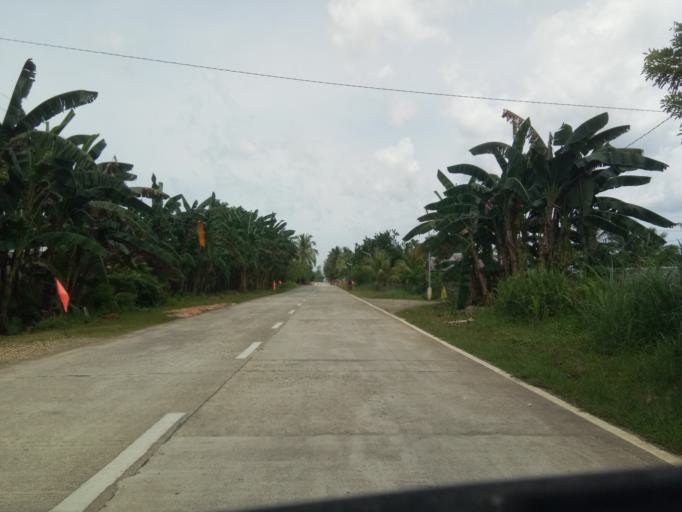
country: PH
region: Caraga
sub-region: Province of Surigao del Norte
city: San Isidro
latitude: 9.9217
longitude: 126.0498
